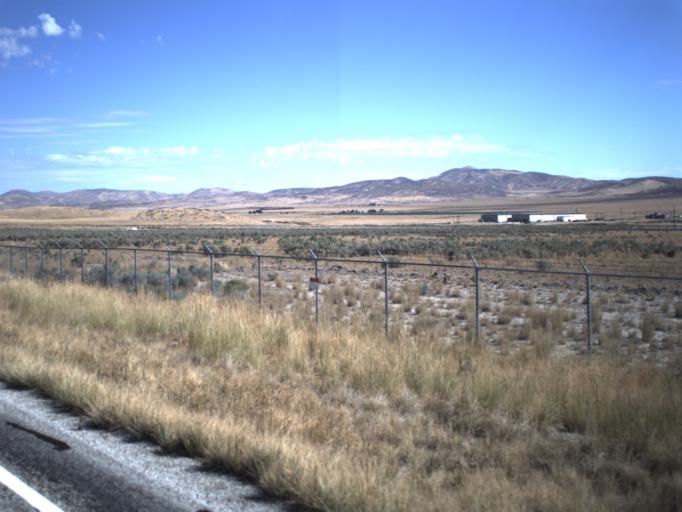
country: US
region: Utah
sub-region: Box Elder County
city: Tremonton
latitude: 41.7142
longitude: -112.4526
